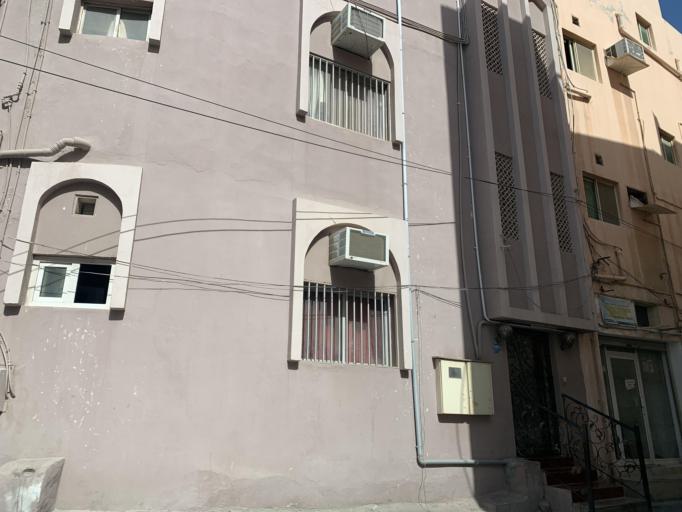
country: BH
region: Muharraq
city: Al Muharraq
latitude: 26.2592
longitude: 50.6101
